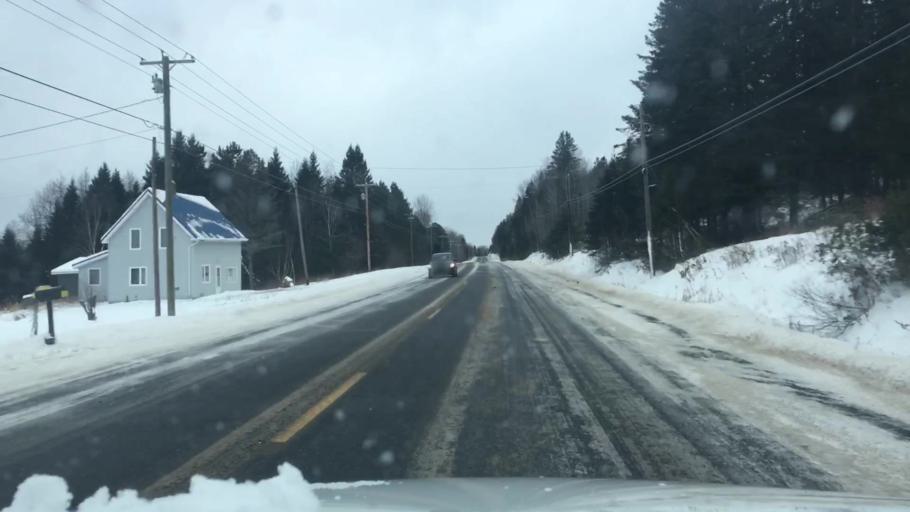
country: US
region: Maine
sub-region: Aroostook County
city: Madawaska
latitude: 47.3307
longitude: -68.1986
